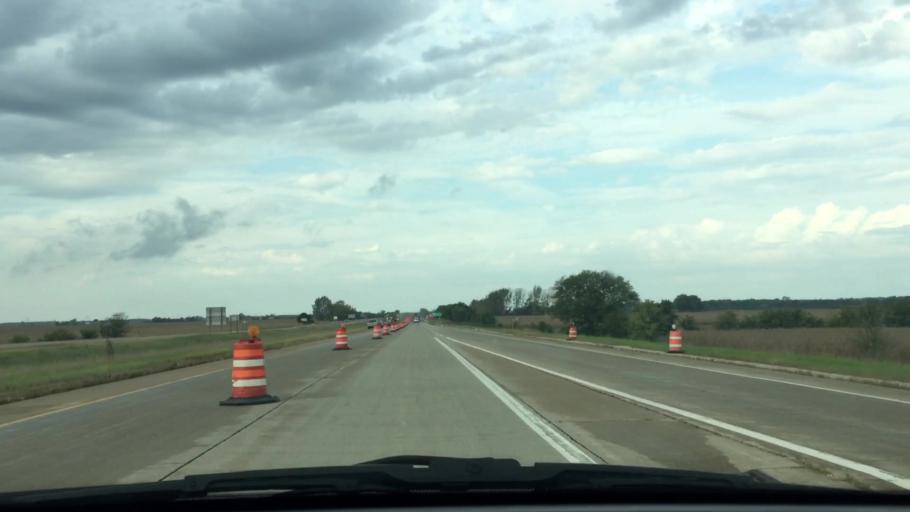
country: US
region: Illinois
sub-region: Whiteside County
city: Prophetstown
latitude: 41.7214
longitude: -89.9714
